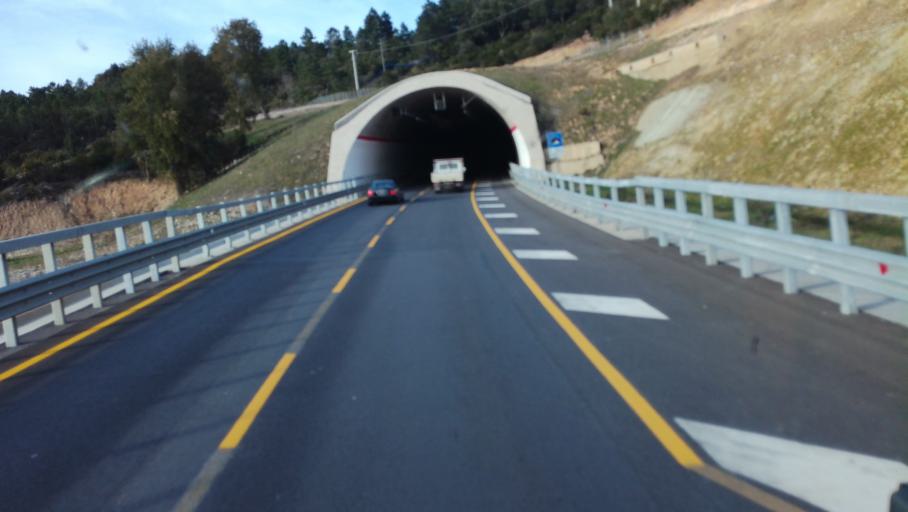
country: IT
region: Tuscany
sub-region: Provincia di Grosseto
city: Civitella Marittima
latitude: 43.0351
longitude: 11.2761
